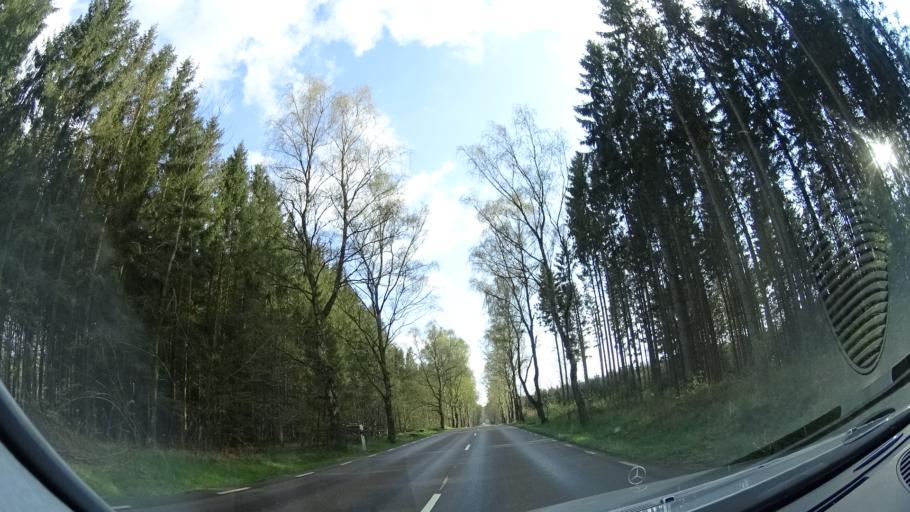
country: SE
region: Skane
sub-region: Klippans Kommun
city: Ljungbyhed
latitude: 56.0584
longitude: 13.2444
